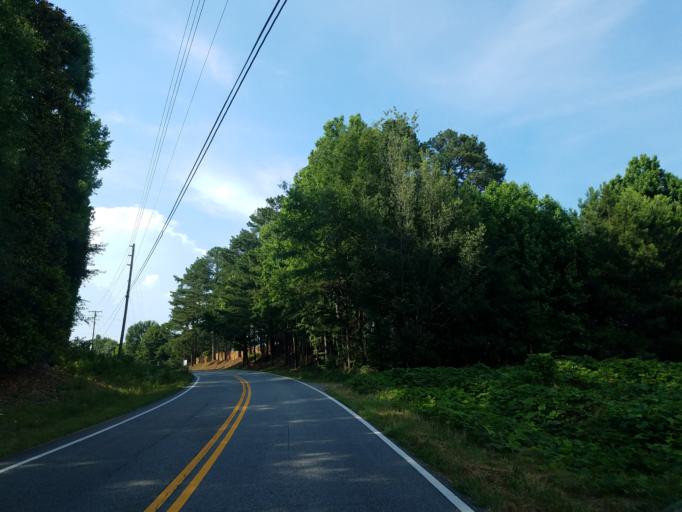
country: US
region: Georgia
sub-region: Forsyth County
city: Cumming
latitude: 34.2902
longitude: -84.0667
